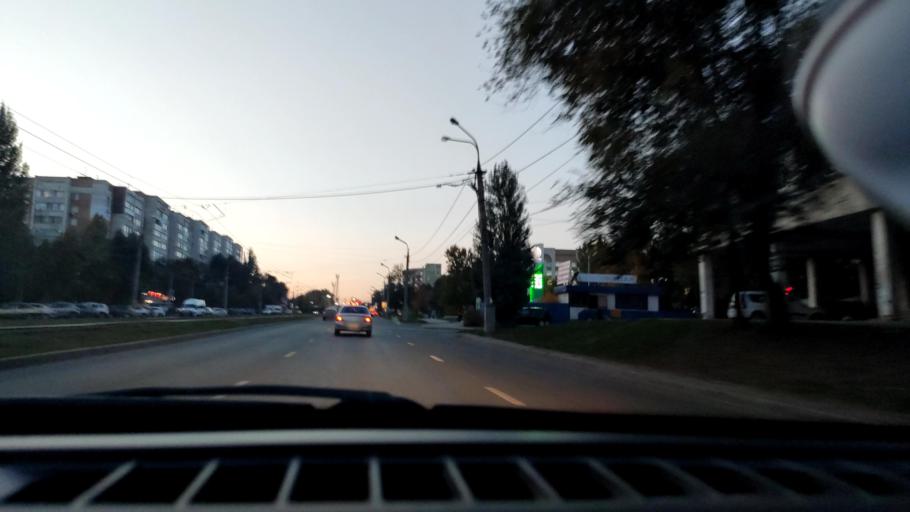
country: RU
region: Samara
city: Samara
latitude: 53.2145
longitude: 50.2254
